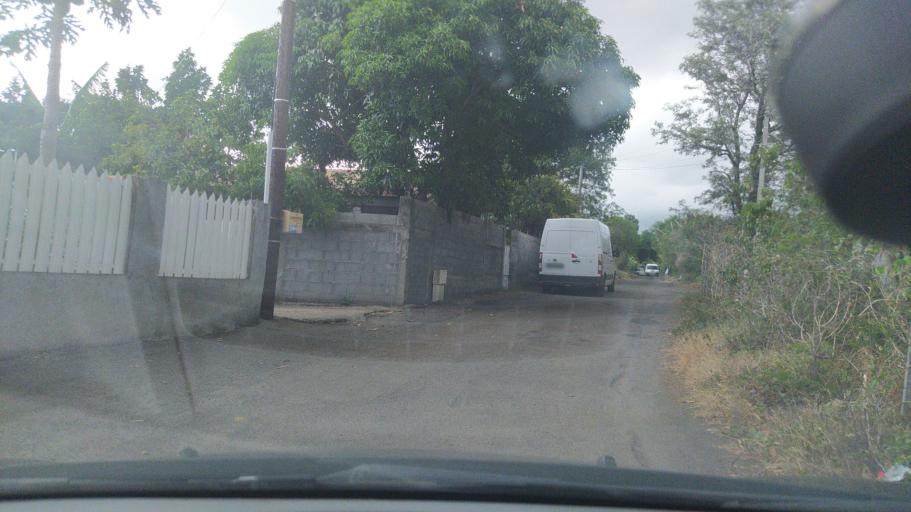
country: RE
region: Reunion
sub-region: Reunion
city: Saint-Pierre
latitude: -21.3048
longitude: 55.4647
